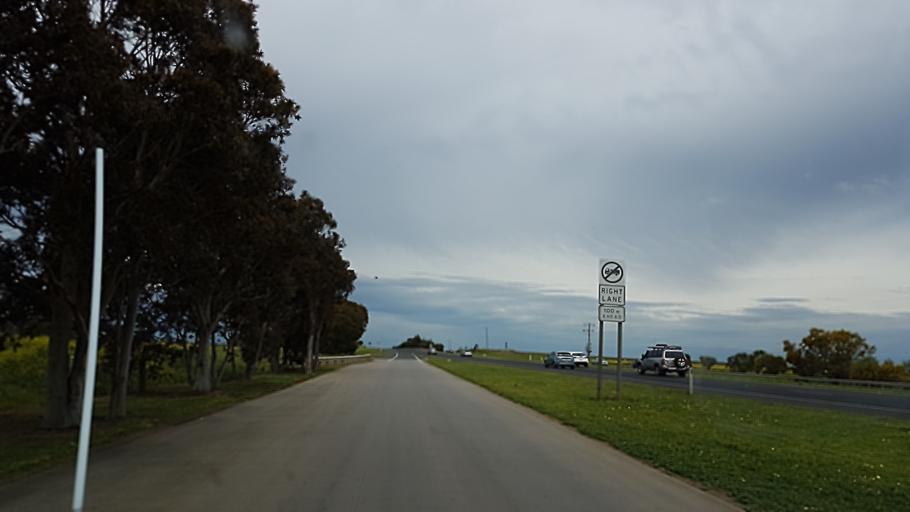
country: AU
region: Victoria
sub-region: Wyndham
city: Little River
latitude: -38.0033
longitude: 144.4902
